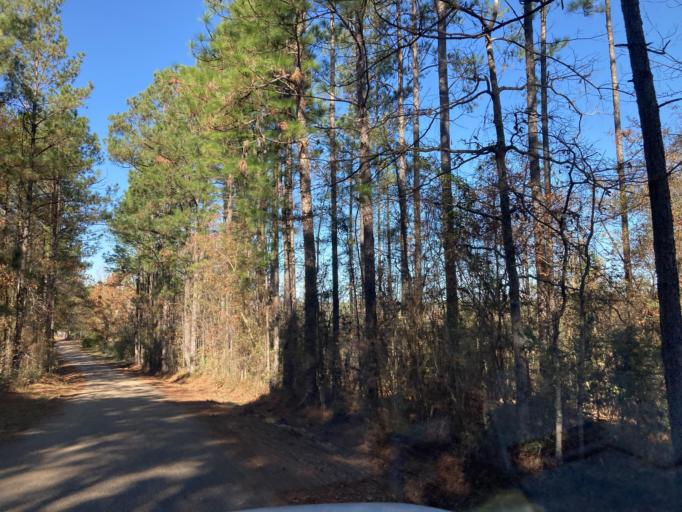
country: US
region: Mississippi
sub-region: Lamar County
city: Sumrall
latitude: 31.2904
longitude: -89.6032
